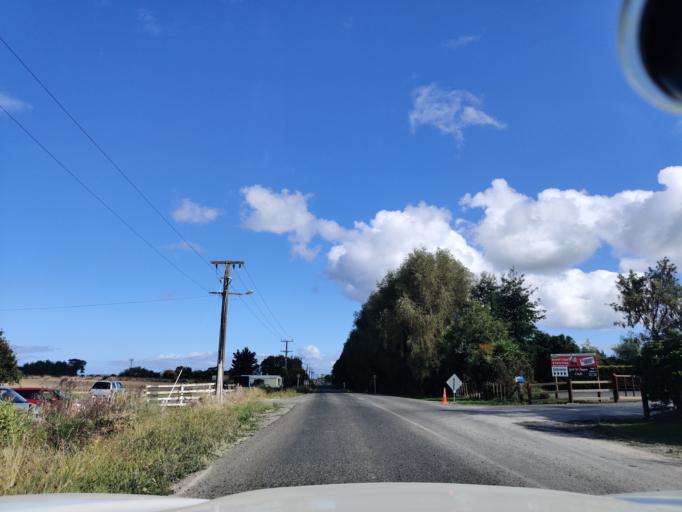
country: NZ
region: Manawatu-Wanganui
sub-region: Horowhenua District
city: Levin
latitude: -40.6512
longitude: 175.2567
